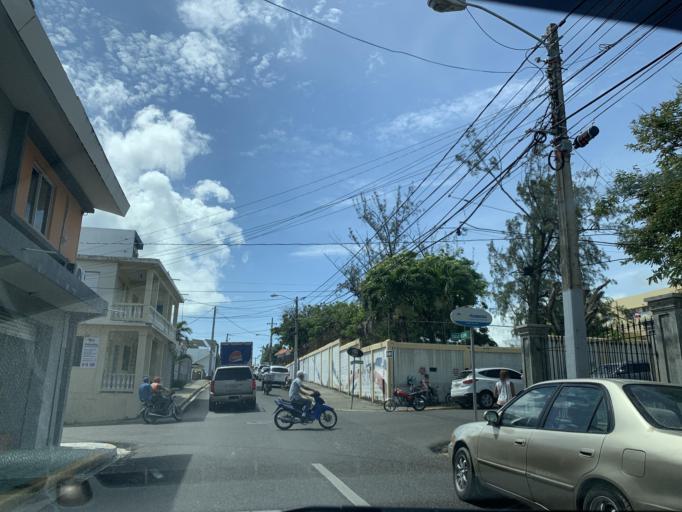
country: DO
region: Puerto Plata
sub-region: Puerto Plata
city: Puerto Plata
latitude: 19.7954
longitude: -70.6883
